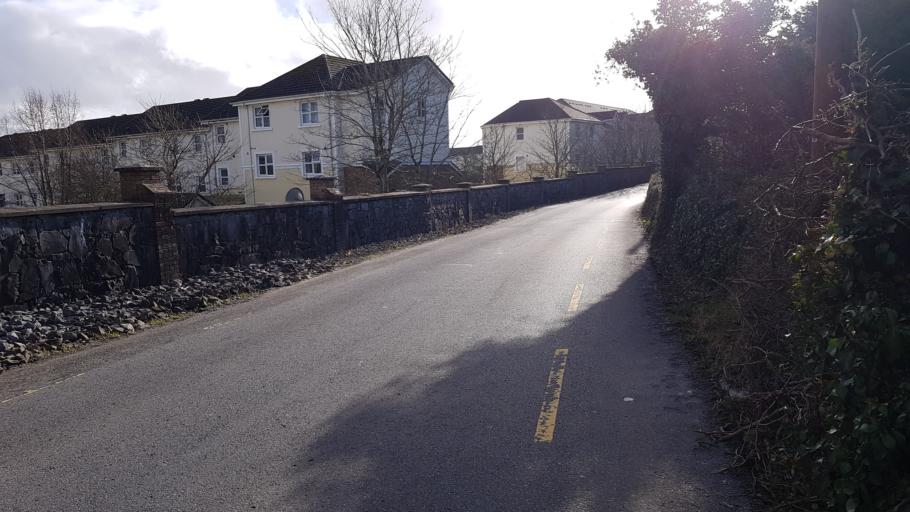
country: IE
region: Connaught
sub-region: County Galway
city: Gaillimh
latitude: 53.2990
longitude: -9.0275
